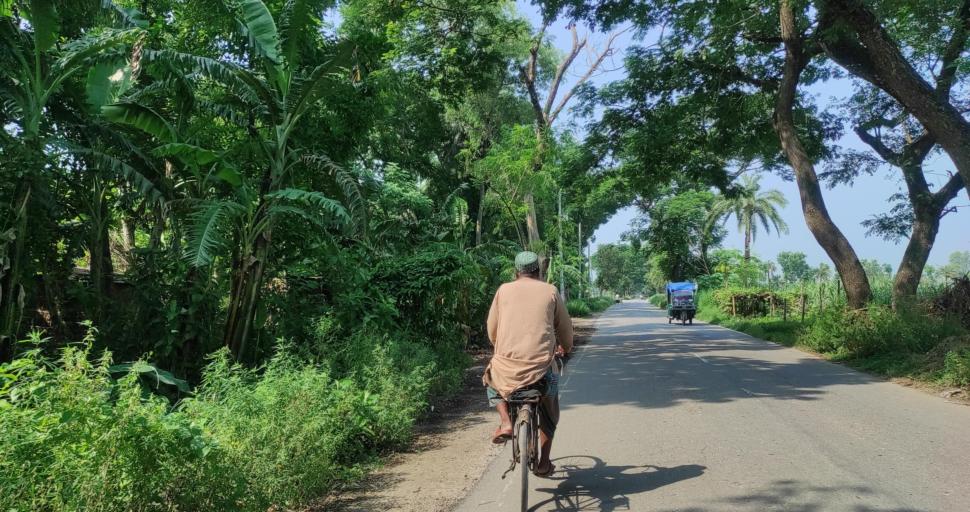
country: BD
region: Rajshahi
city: Ishurdi
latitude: 24.2717
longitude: 89.0553
